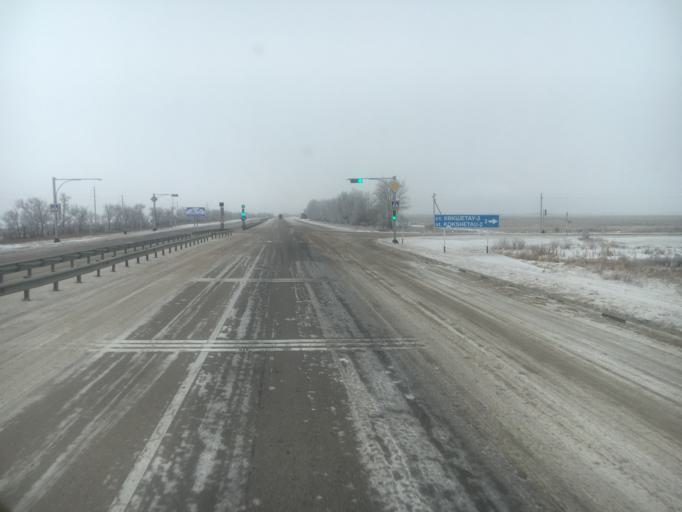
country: KZ
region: Aqmola
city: Akkol'
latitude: 53.3401
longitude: 69.5046
